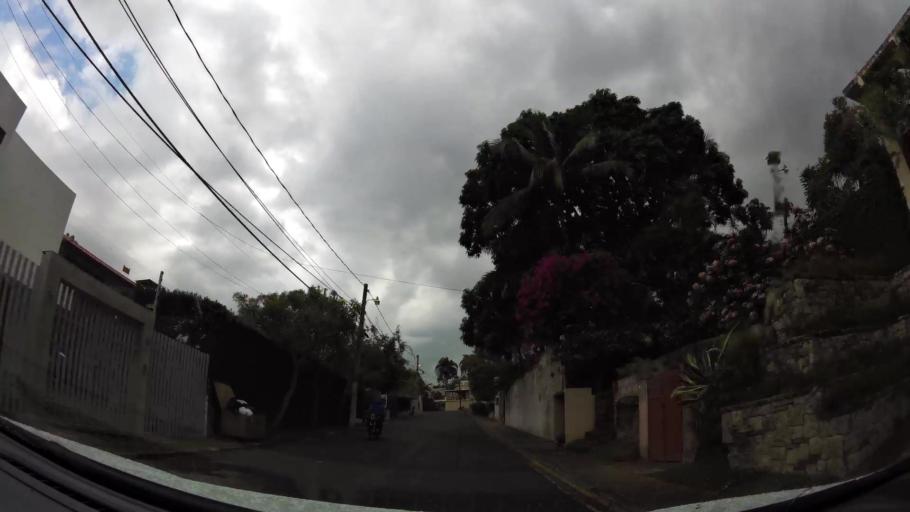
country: DO
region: Nacional
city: La Agustina
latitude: 18.4994
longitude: -69.9394
